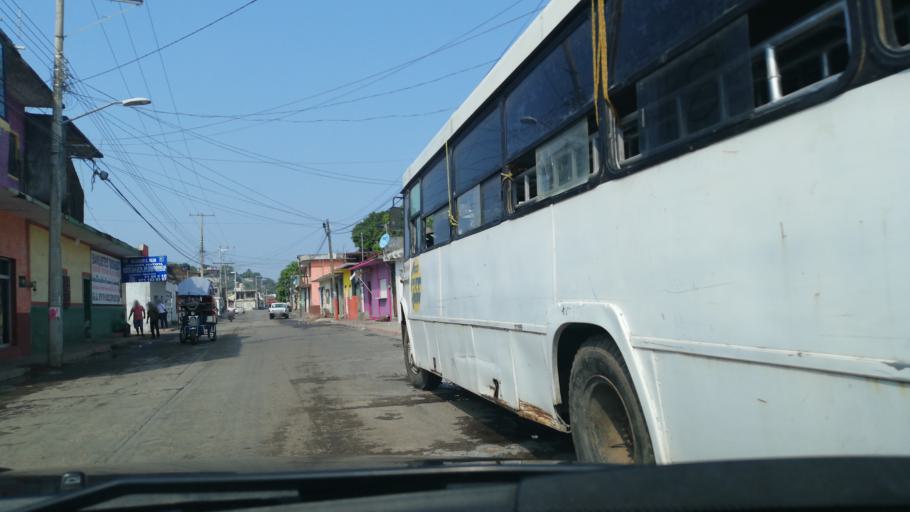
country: MX
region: Oaxaca
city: San Blas Atempa
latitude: 16.3380
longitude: -95.2253
